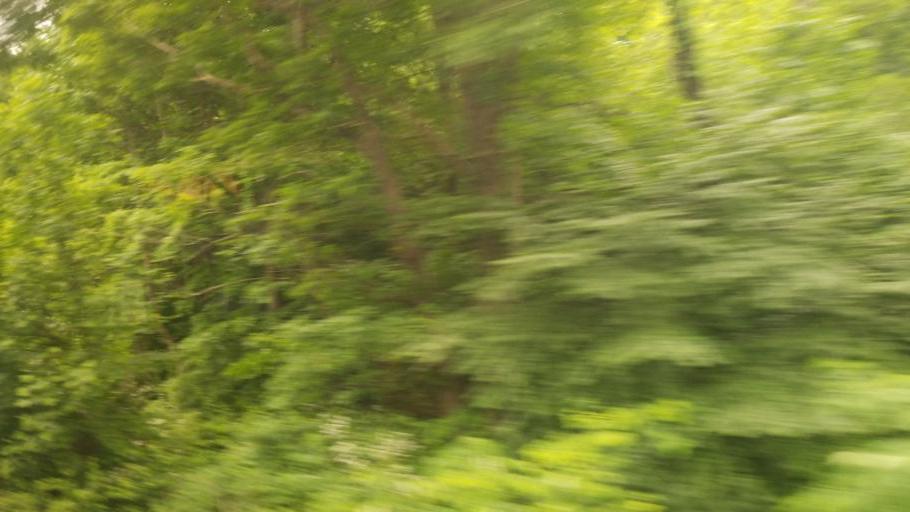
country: US
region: Pennsylvania
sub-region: Somerset County
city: Milford
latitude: 39.8275
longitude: -79.3055
